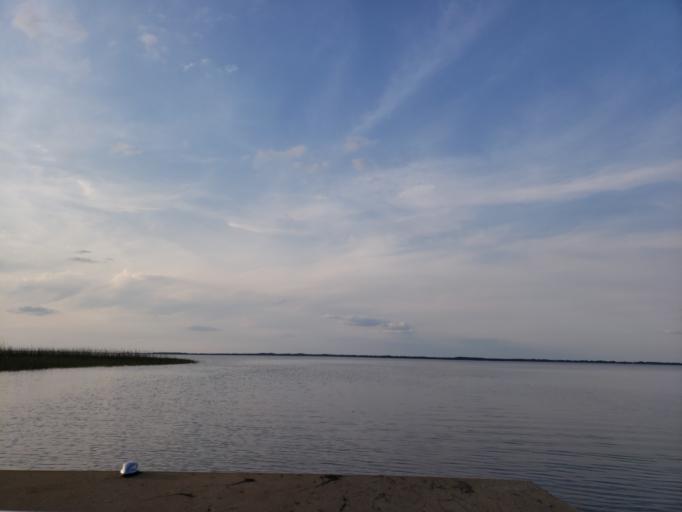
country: US
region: Florida
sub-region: Osceola County
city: Poinciana
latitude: 28.1426
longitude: -81.3518
